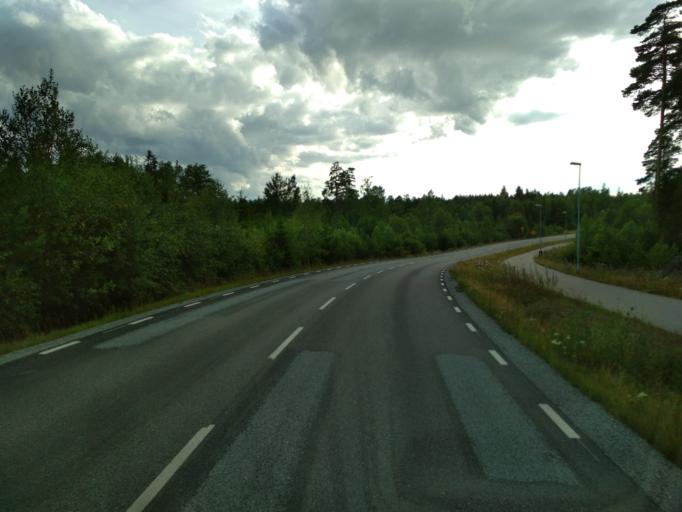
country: SE
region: Uppsala
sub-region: Habo Kommun
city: Balsta
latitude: 59.6814
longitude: 17.5986
